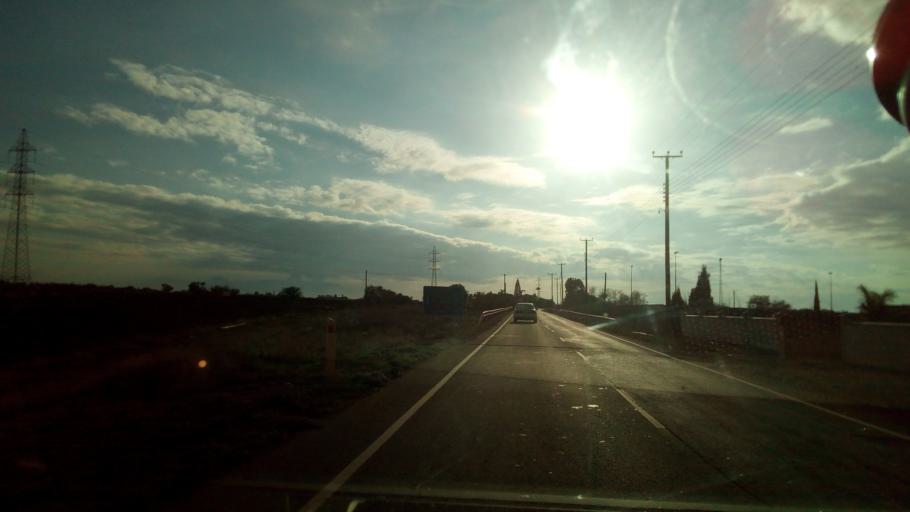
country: CY
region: Ammochostos
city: Avgorou
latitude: 35.0219
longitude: 33.8311
